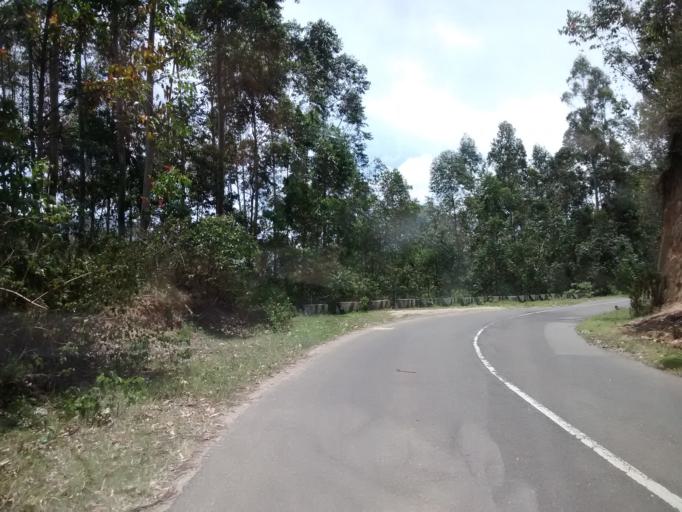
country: IN
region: Kerala
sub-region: Idukki
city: Munnar
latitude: 10.1377
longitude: 77.1877
